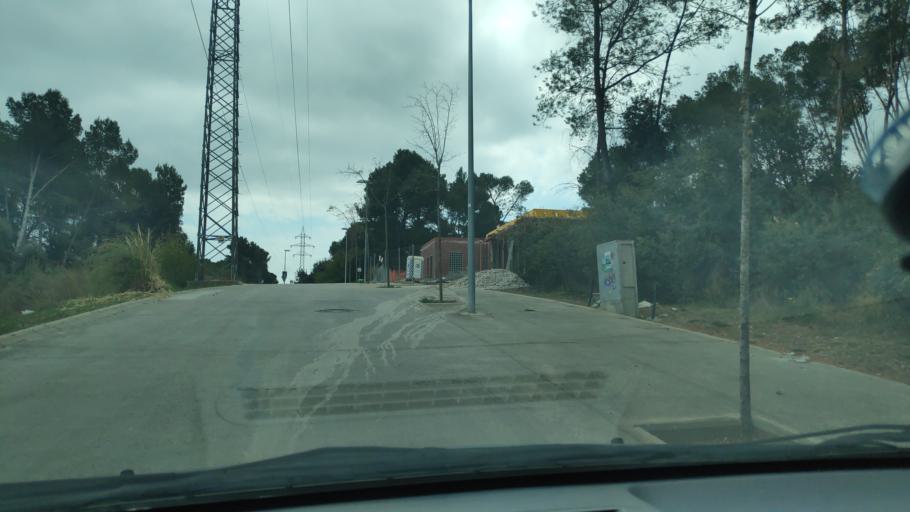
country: ES
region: Catalonia
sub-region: Provincia de Barcelona
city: Sant Quirze del Valles
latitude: 41.5178
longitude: 2.0896
